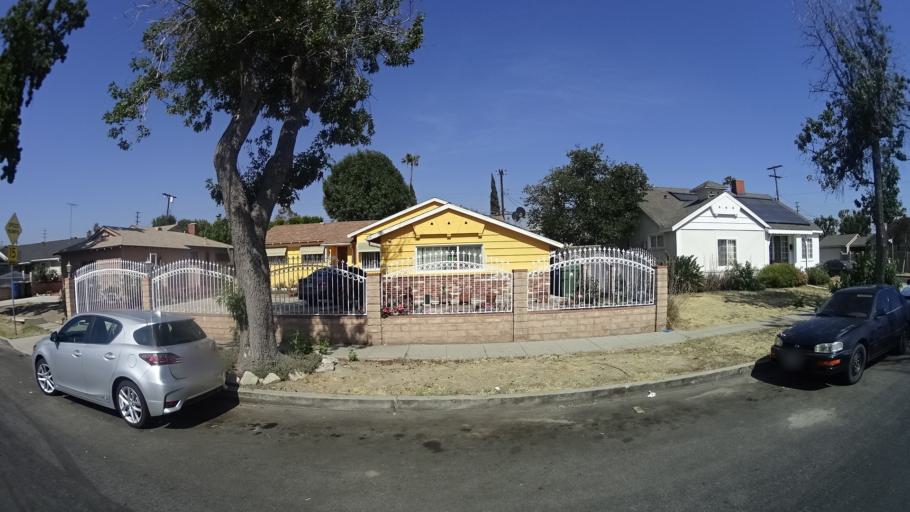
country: US
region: California
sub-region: Los Angeles County
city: Van Nuys
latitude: 34.1979
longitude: -118.4236
